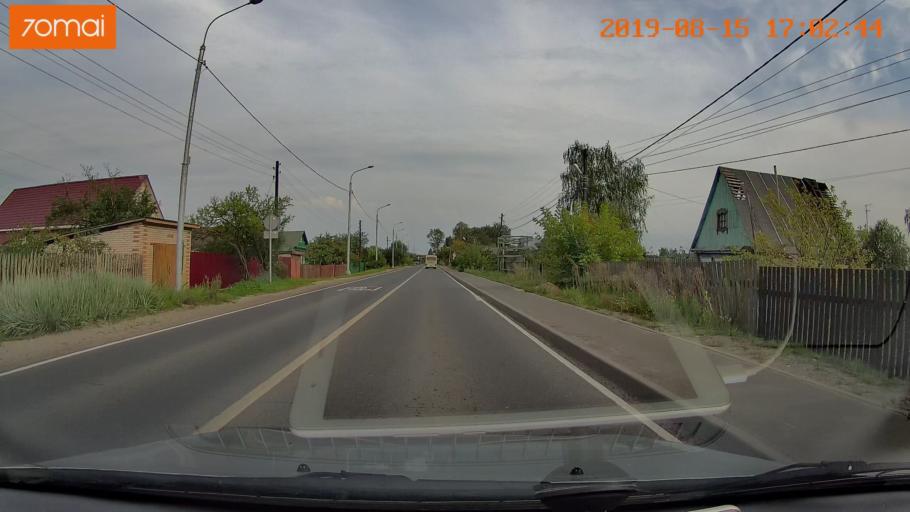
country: RU
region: Moskovskaya
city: Malyshevo
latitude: 55.4840
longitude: 38.3955
